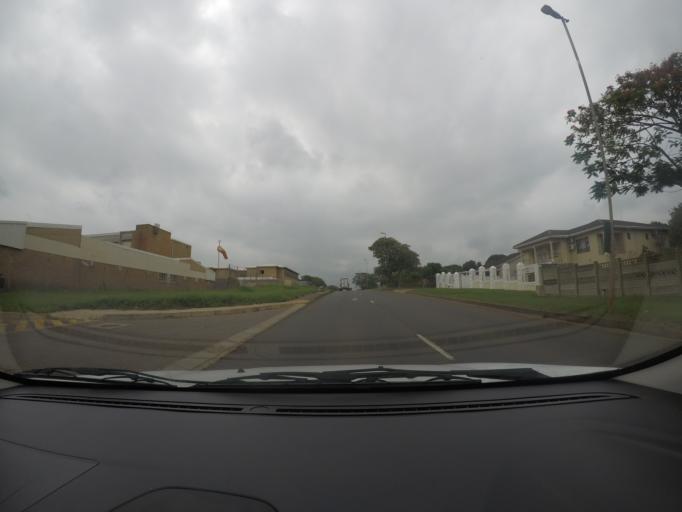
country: ZA
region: KwaZulu-Natal
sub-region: uThungulu District Municipality
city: Empangeni
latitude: -28.7398
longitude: 31.8982
